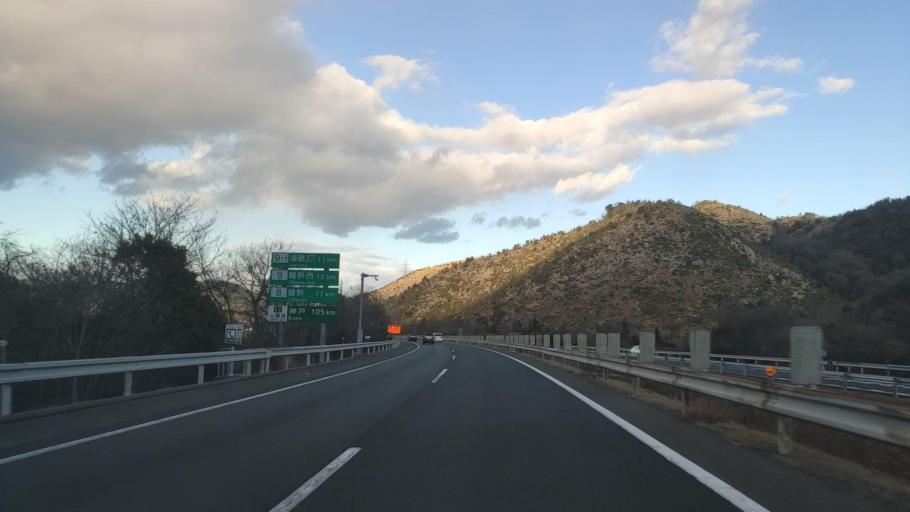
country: JP
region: Hyogo
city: Kariya
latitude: 34.7804
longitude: 134.3954
